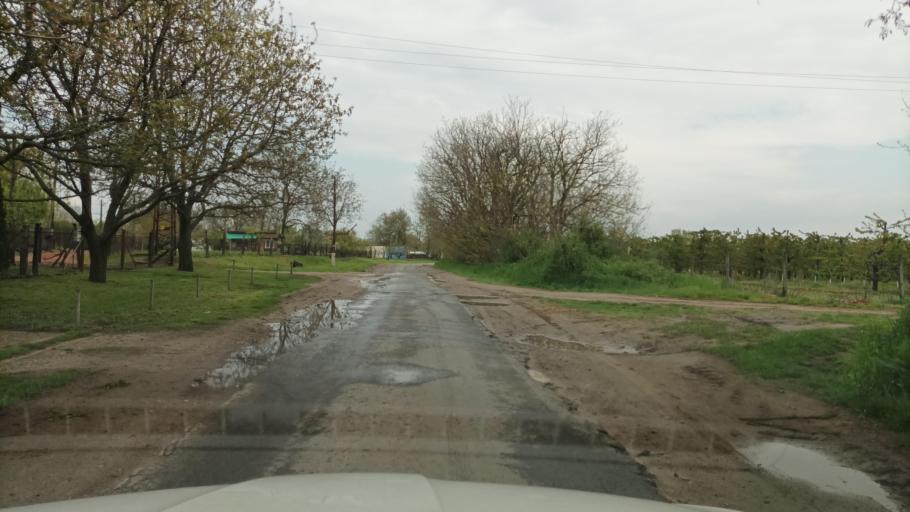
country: HU
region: Pest
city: Nagykoros
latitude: 47.0137
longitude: 19.7938
